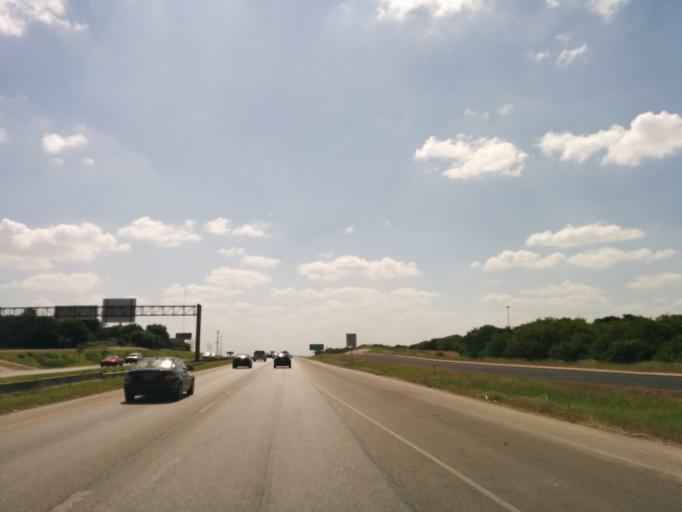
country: US
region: Texas
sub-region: Bexar County
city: Live Oak
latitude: 29.6028
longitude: -98.3734
